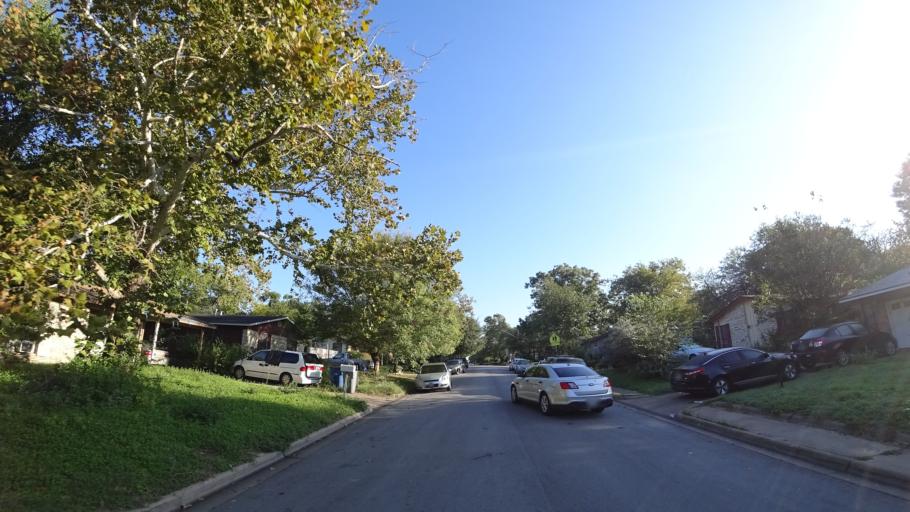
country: US
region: Texas
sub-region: Travis County
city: Wells Branch
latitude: 30.3582
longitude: -97.6963
